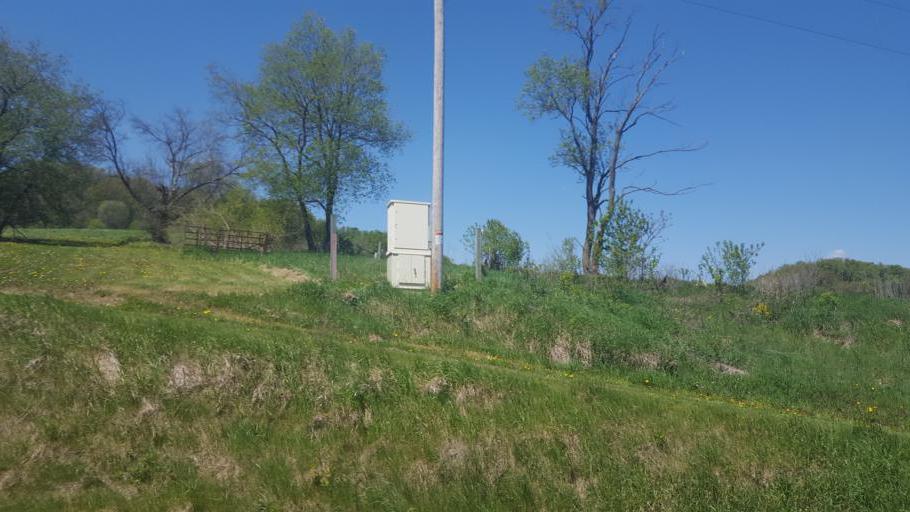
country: US
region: Wisconsin
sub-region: Vernon County
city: Hillsboro
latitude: 43.5750
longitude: -90.4420
